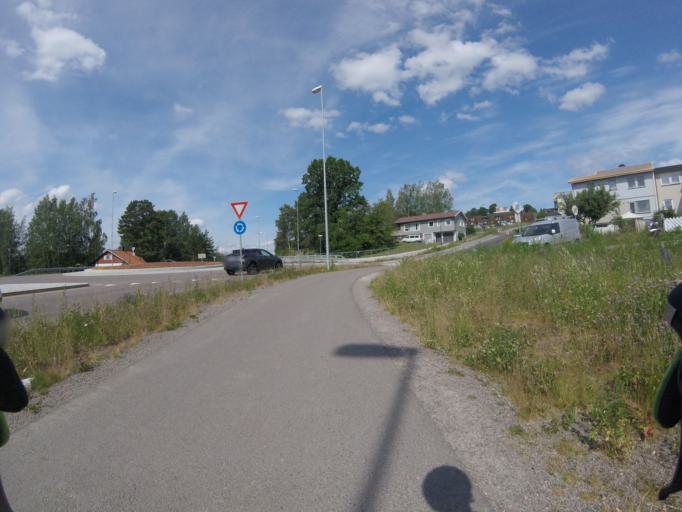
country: NO
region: Akershus
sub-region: Skedsmo
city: Lillestrom
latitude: 59.9759
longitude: 11.0260
